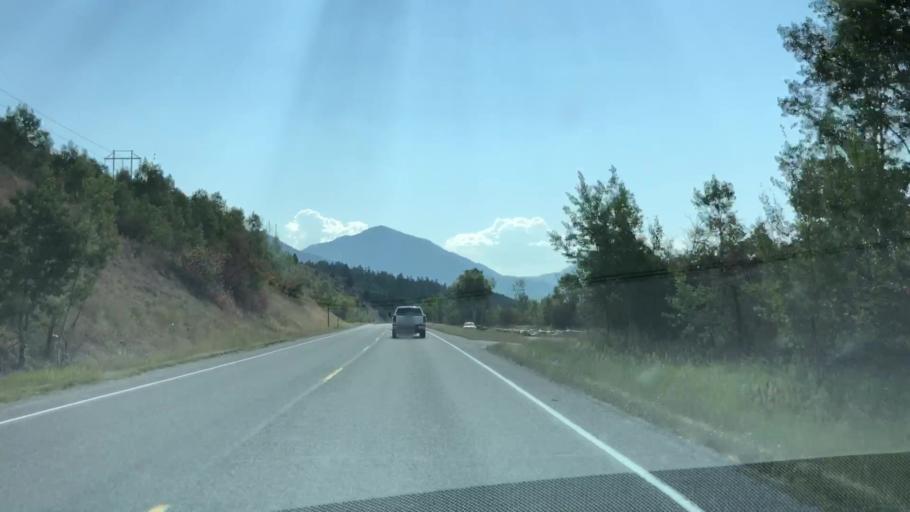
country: US
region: Wyoming
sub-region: Teton County
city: Hoback
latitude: 43.2061
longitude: -111.0522
